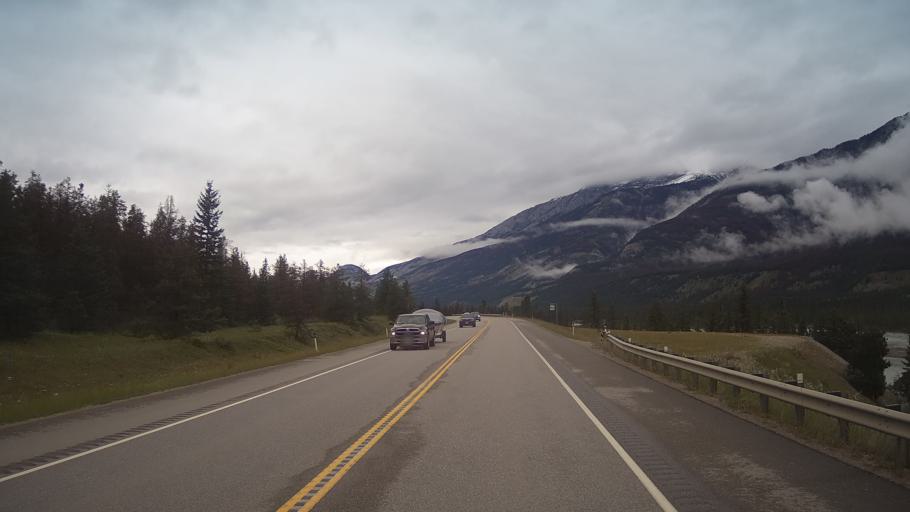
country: CA
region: Alberta
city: Jasper Park Lodge
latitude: 52.9452
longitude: -118.0397
